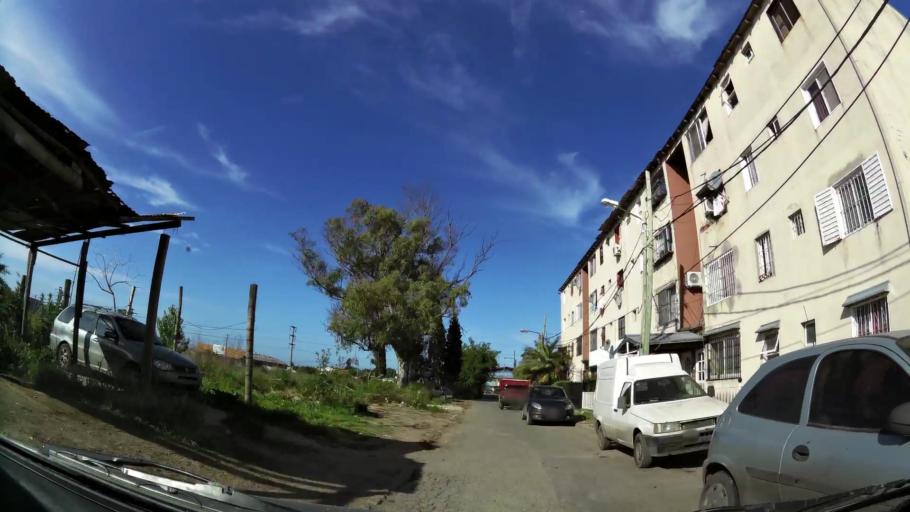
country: AR
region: Buenos Aires
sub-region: Partido de Quilmes
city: Quilmes
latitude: -34.7805
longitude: -58.2357
